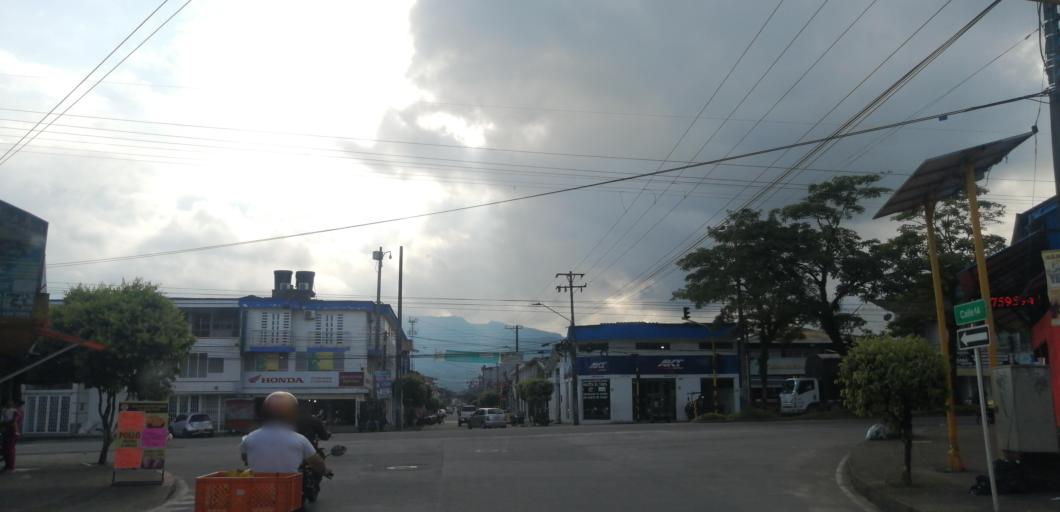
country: CO
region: Meta
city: Acacias
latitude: 3.9872
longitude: -73.7657
